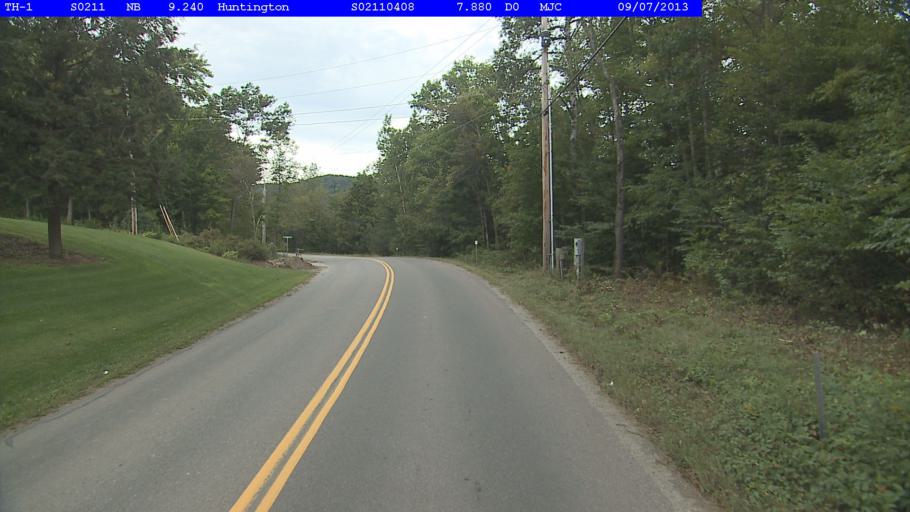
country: US
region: Vermont
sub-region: Chittenden County
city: Hinesburg
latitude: 44.3314
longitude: -72.9896
